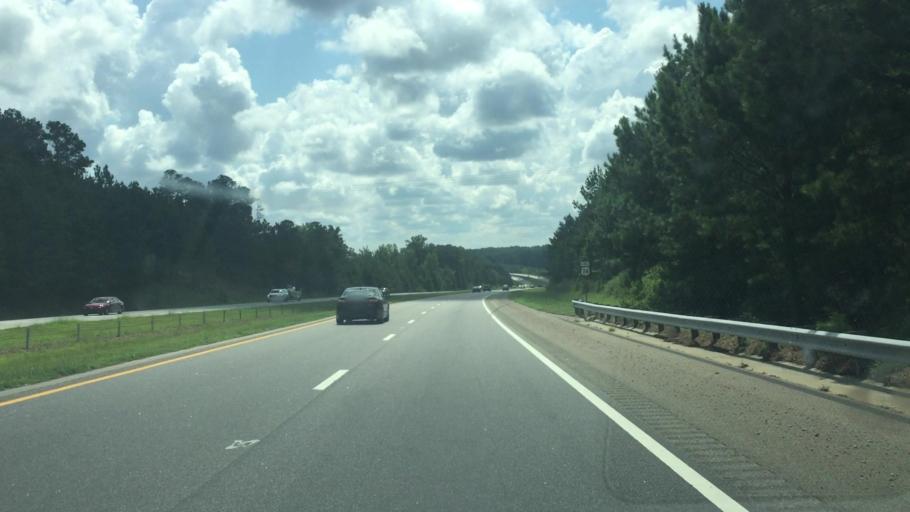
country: US
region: North Carolina
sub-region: Richmond County
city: Cordova
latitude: 34.9283
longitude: -79.8233
